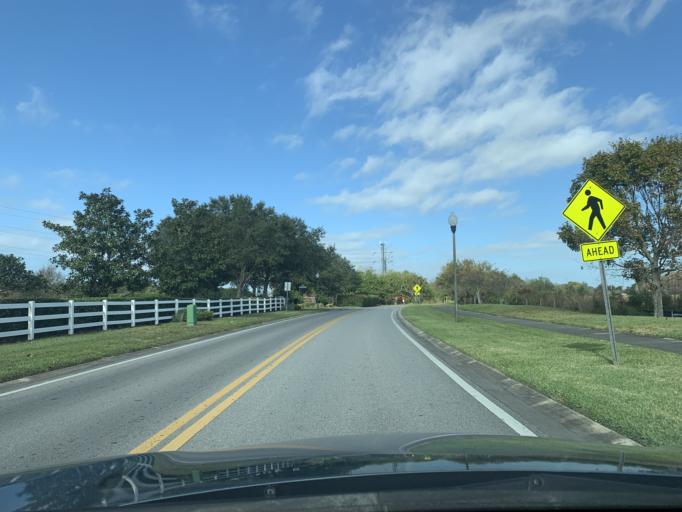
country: US
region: Florida
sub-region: Pasco County
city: Trinity
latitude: 28.2001
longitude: -82.6803
